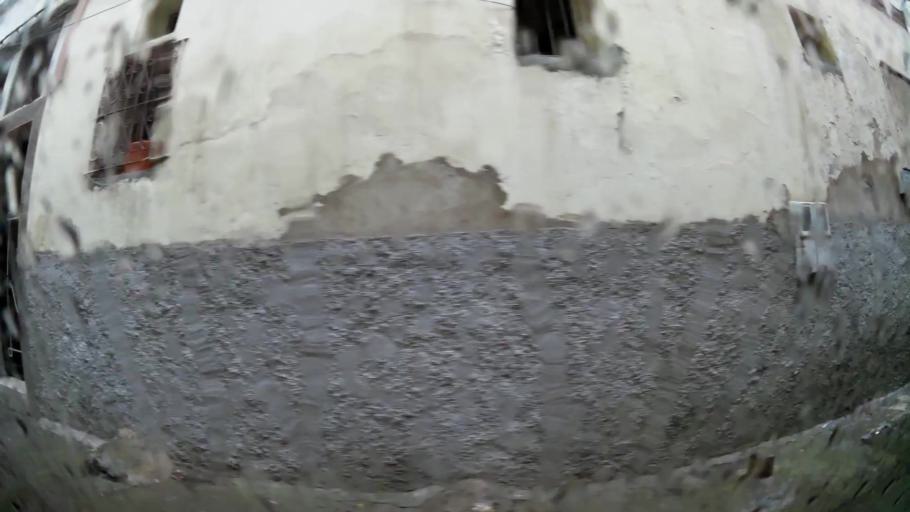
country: MA
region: Grand Casablanca
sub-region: Casablanca
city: Casablanca
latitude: 33.5759
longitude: -7.6047
